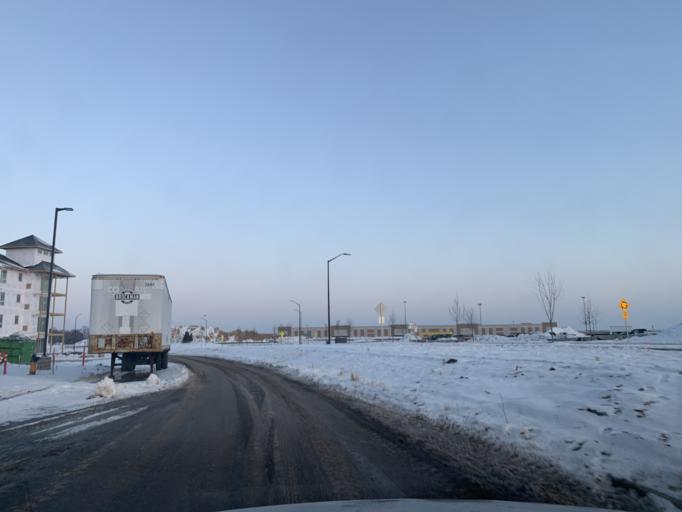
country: US
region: Minnesota
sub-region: Scott County
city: Shakopee
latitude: 44.7906
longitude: -93.4868
